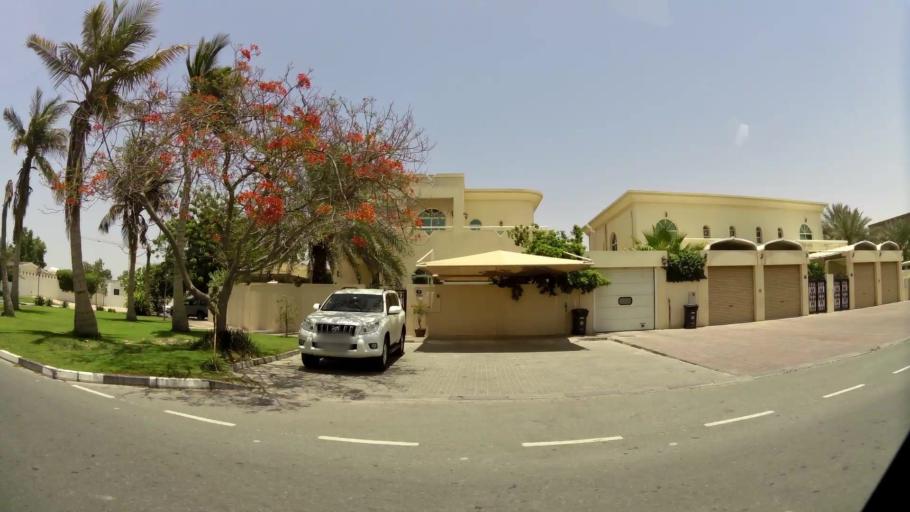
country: AE
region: Dubai
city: Dubai
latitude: 25.1764
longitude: 55.2369
